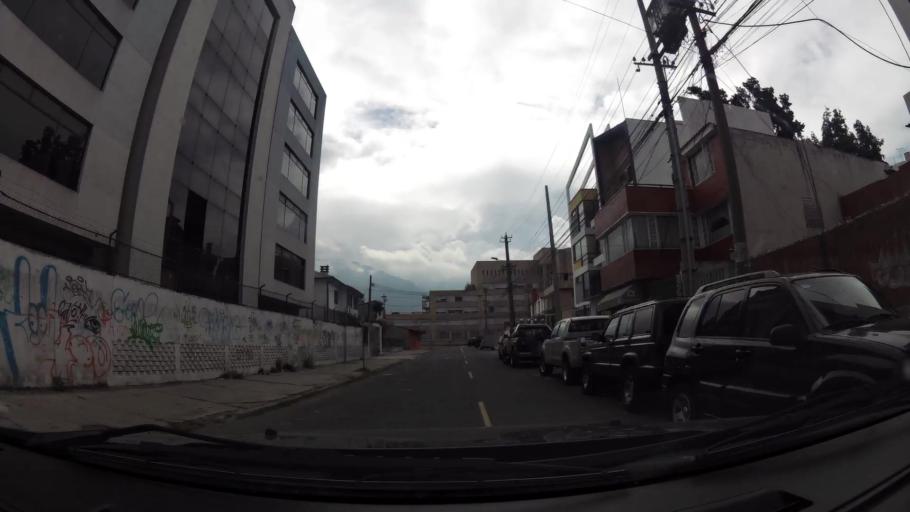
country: EC
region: Pichincha
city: Quito
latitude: -0.2104
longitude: -78.4862
